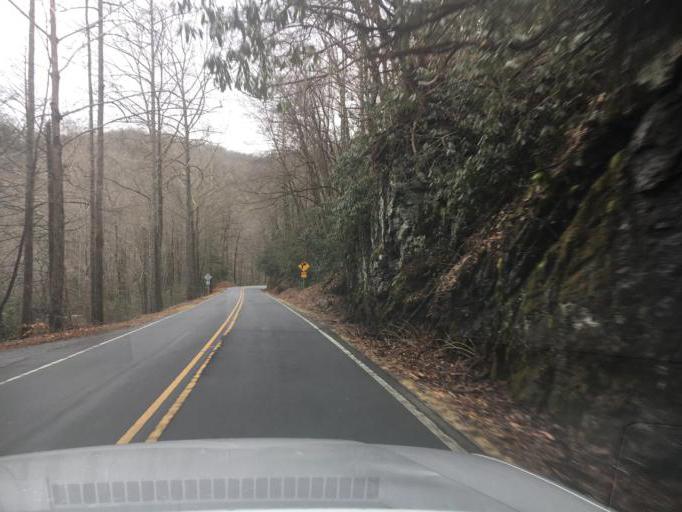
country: US
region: North Carolina
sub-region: Transylvania County
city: Brevard
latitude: 35.2833
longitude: -82.7548
